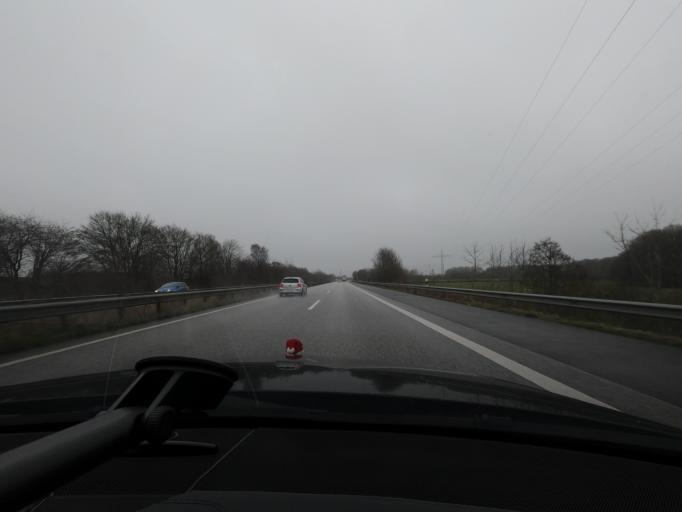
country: DE
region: Schleswig-Holstein
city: Bollingstedt
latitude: 54.5938
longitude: 9.4587
